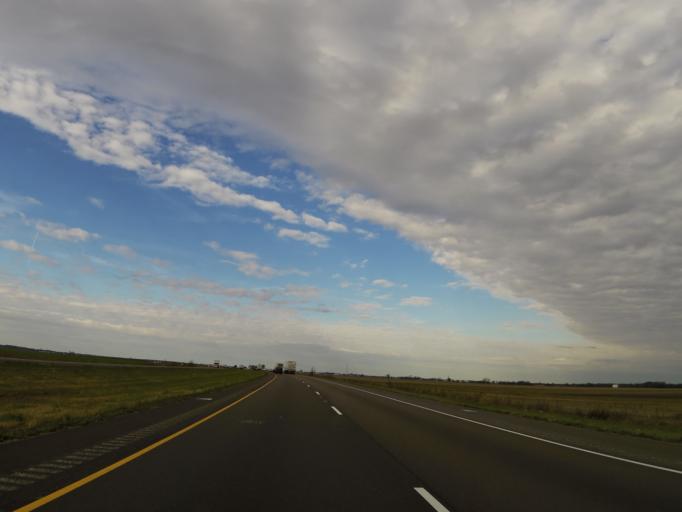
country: US
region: Illinois
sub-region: Washington County
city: Okawville
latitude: 38.4260
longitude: -89.4614
